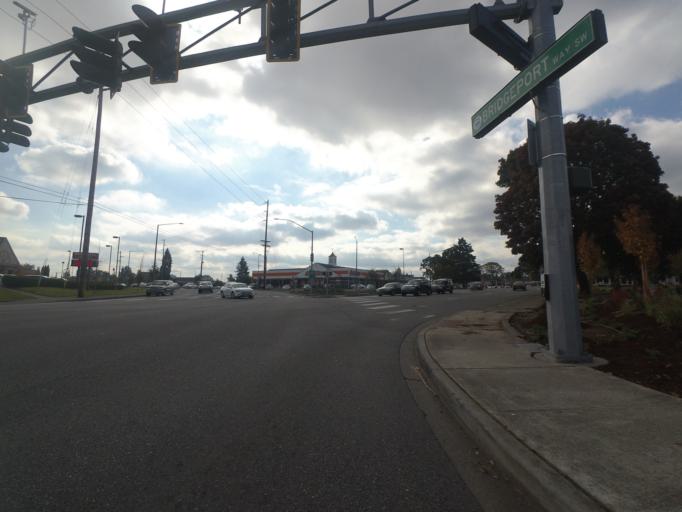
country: US
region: Washington
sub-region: Pierce County
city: Lakewood
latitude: 47.1720
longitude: -122.5186
